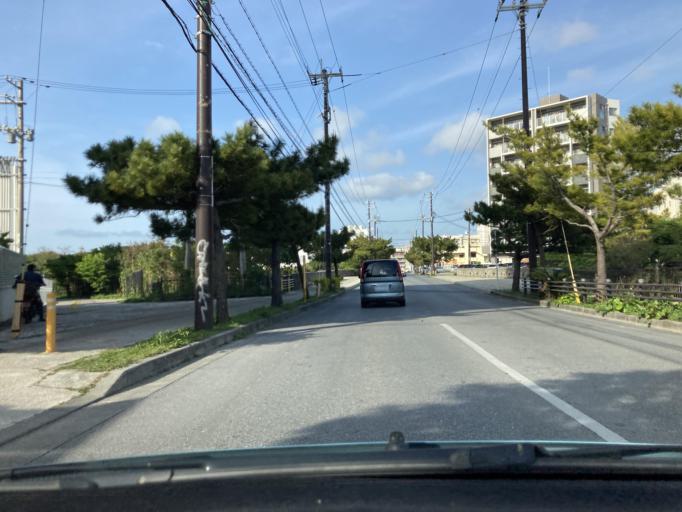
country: JP
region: Okinawa
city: Naha-shi
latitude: 26.2349
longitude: 127.6956
